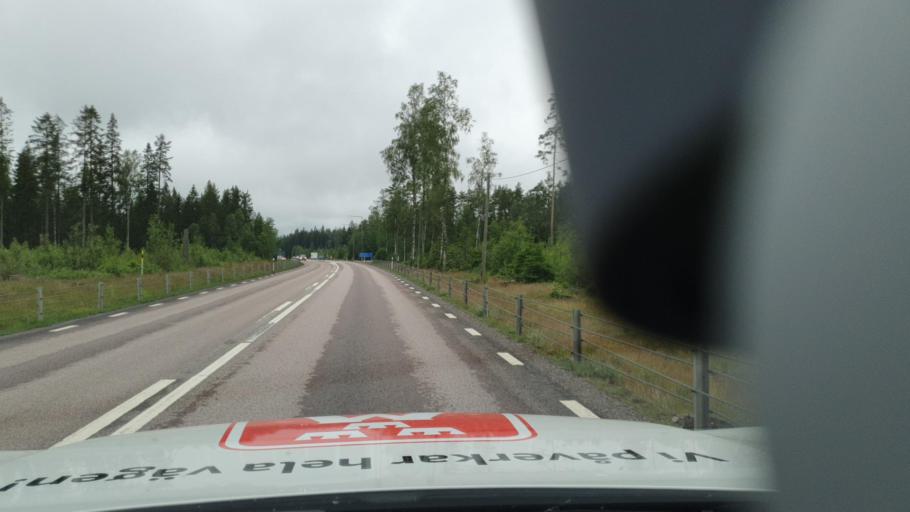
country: SE
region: Vaermland
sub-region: Kristinehamns Kommun
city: Bjorneborg
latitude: 59.2501
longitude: 14.1774
